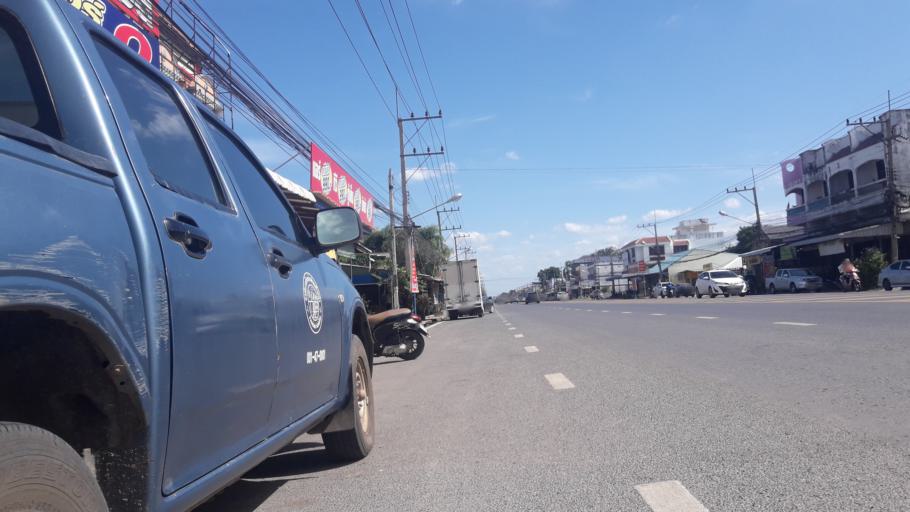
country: TH
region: Phichit
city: Thap Khlo
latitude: 16.1671
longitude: 100.5810
